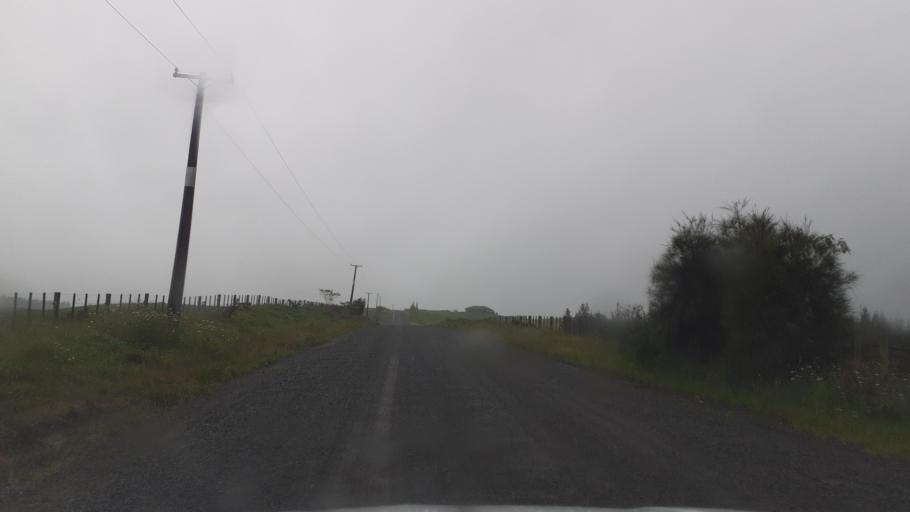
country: NZ
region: Northland
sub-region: Far North District
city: Kerikeri
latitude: -35.2242
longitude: 173.8744
